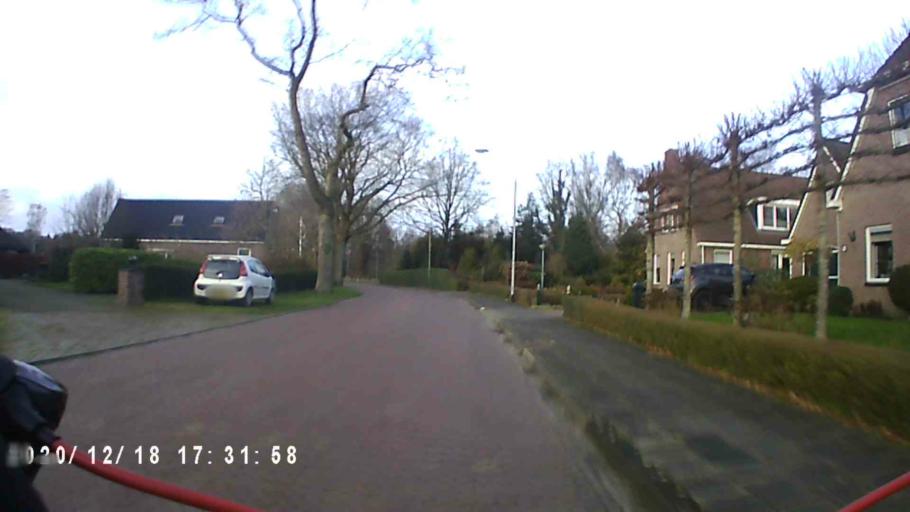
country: NL
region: Drenthe
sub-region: Gemeente Tynaarlo
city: Vries
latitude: 53.0797
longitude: 6.5755
